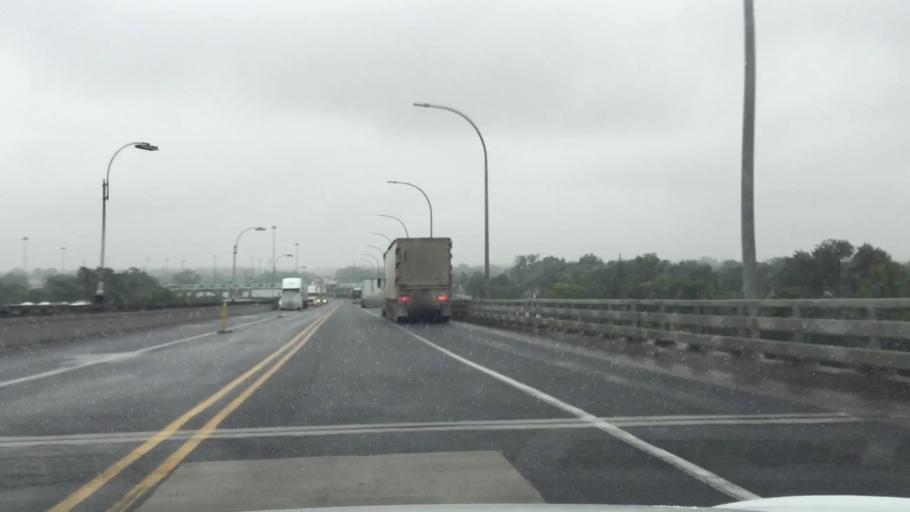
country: US
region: Michigan
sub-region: Wayne County
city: Detroit
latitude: 42.3052
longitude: -83.0697
